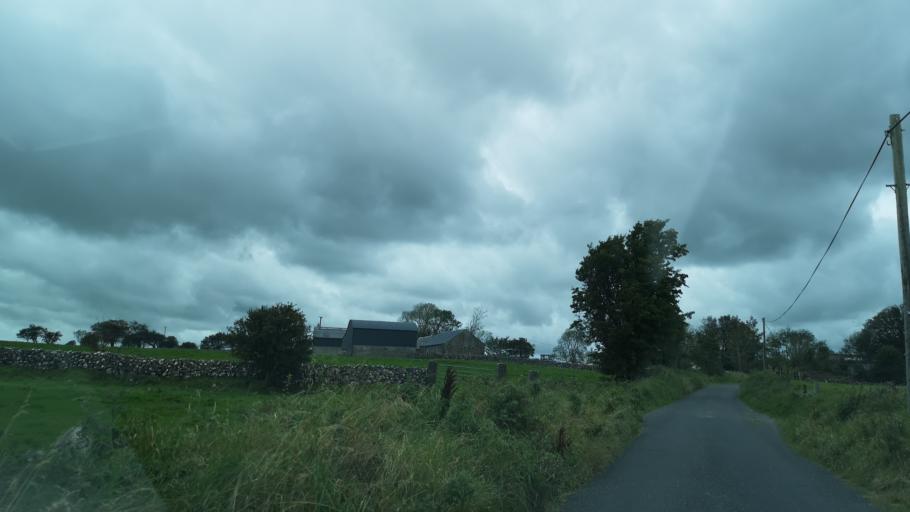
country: IE
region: Connaught
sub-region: County Galway
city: Athenry
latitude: 53.3229
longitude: -8.7292
